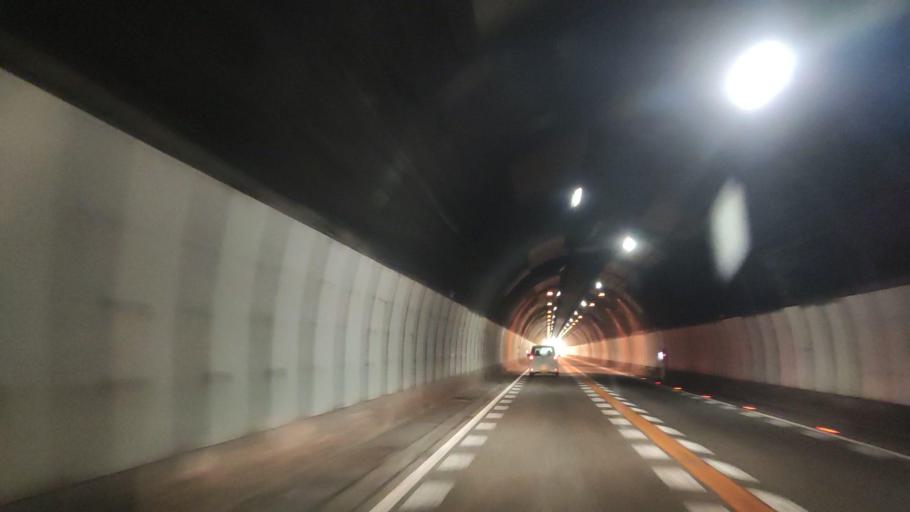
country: JP
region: Hyogo
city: Toyooka
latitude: 35.4843
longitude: 134.5787
